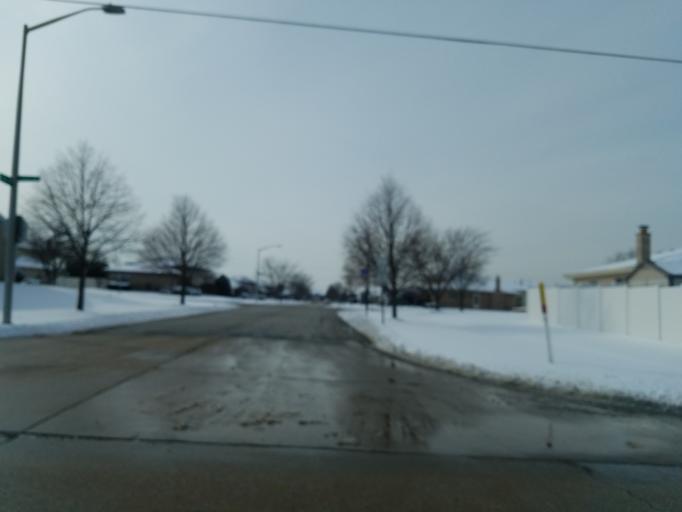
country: US
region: Illinois
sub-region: Cook County
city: Orland Hills
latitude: 41.5977
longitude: -87.8136
